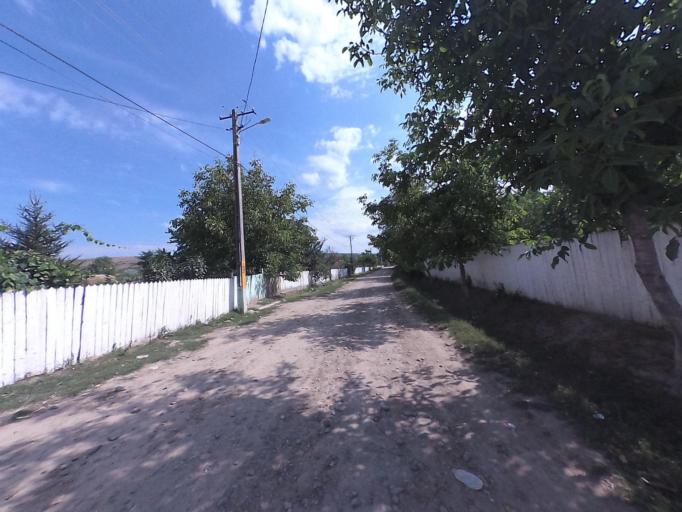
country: RO
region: Vaslui
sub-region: Comuna Osesti
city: Buda
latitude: 46.7614
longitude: 27.4138
